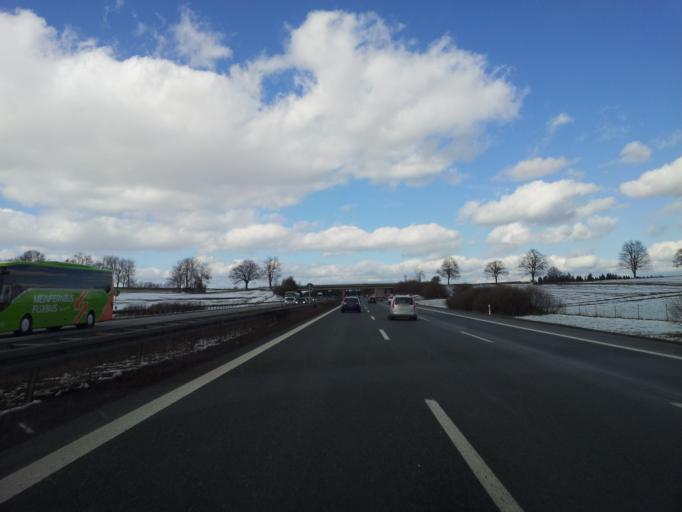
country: DE
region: Bavaria
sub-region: Upper Franconia
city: Gefrees
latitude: 50.1493
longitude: 11.7472
